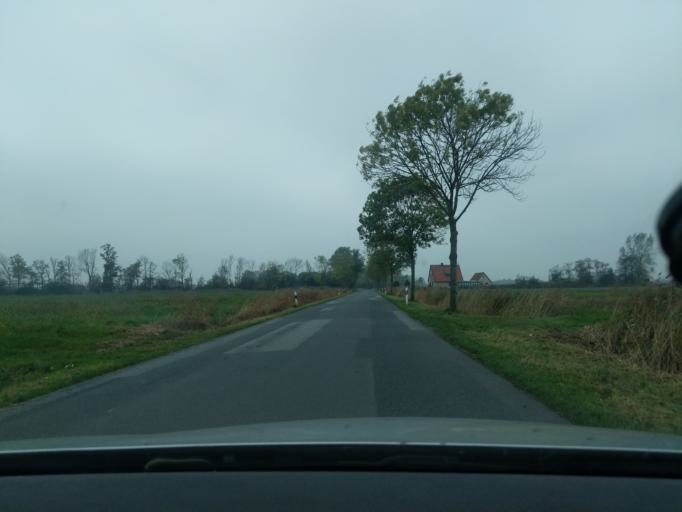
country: DE
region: Lower Saxony
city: Nordleda
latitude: 53.8248
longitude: 8.7953
